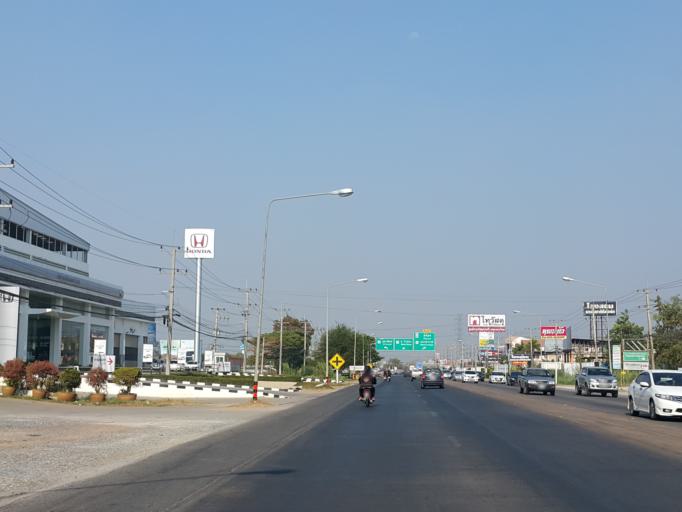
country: TH
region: Phitsanulok
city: Phitsanulok
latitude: 16.8176
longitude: 100.3259
